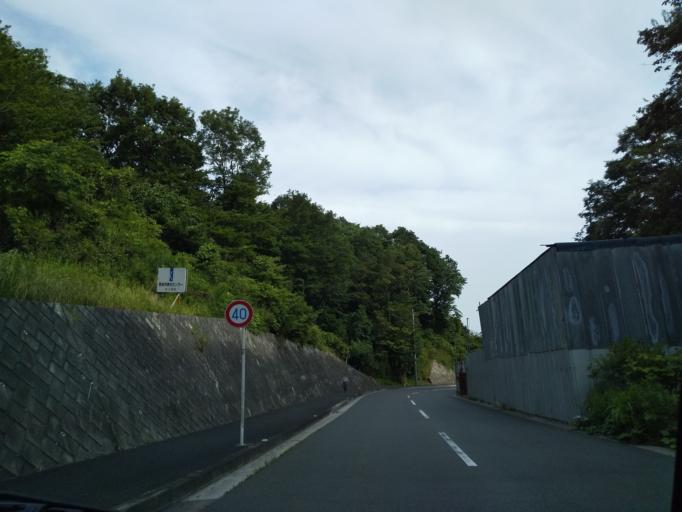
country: JP
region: Kanagawa
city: Atsugi
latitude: 35.4856
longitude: 139.3056
